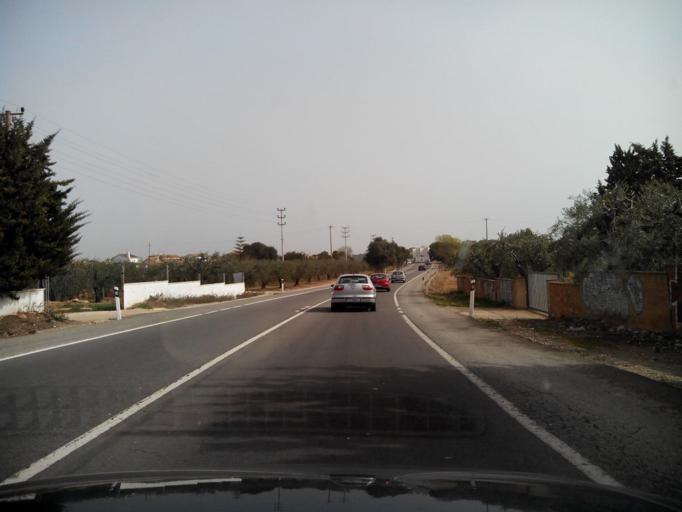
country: ES
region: Catalonia
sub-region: Provincia de Tarragona
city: Creixell
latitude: 41.1663
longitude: 1.4518
